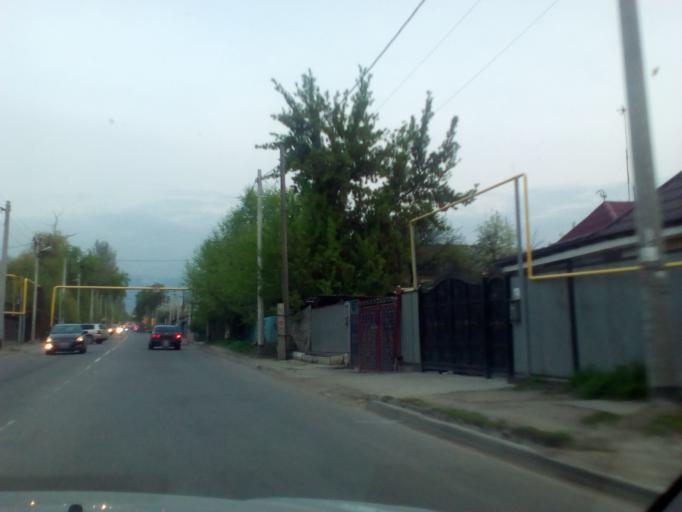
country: KZ
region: Almaty Qalasy
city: Almaty
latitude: 43.2322
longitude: 76.8260
